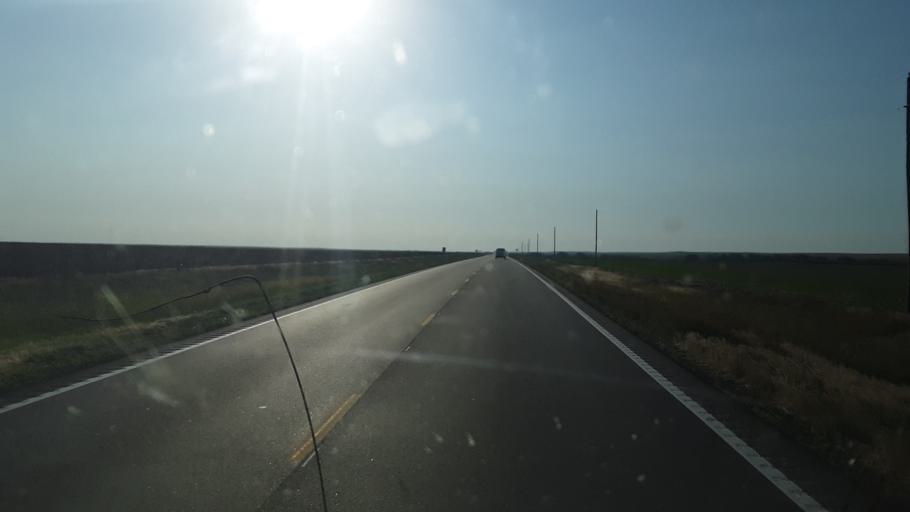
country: US
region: Kansas
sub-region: Hodgeman County
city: Jetmore
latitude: 38.0727
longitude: -100.0237
